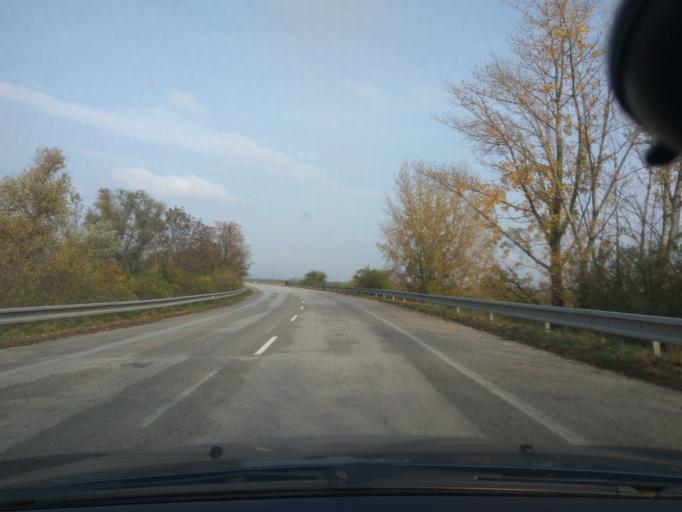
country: SK
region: Trnavsky
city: Vrbove
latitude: 48.6326
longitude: 17.7541
